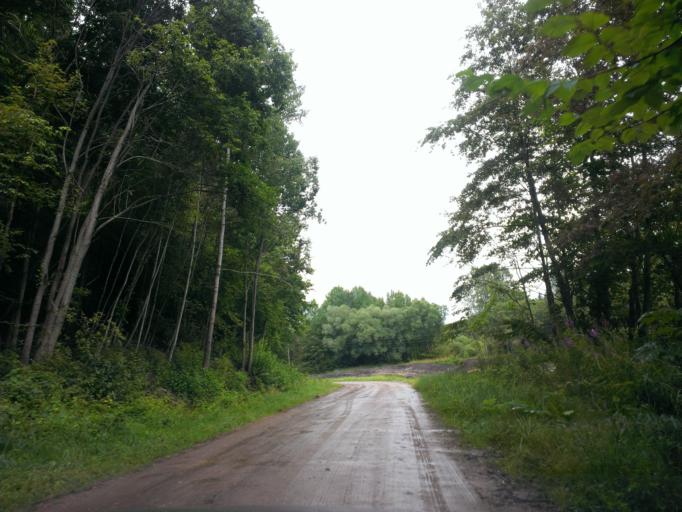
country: LV
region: Ligatne
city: Ligatne
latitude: 57.2131
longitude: 25.0098
